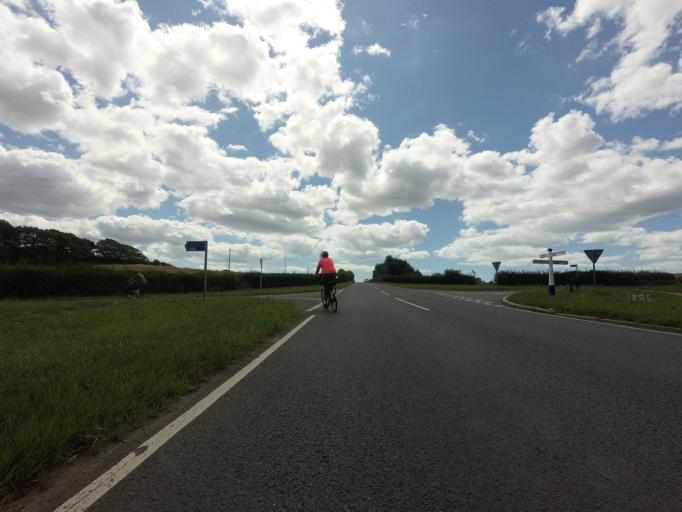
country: GB
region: England
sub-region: East Sussex
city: Seaford
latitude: 50.8374
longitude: 0.1654
